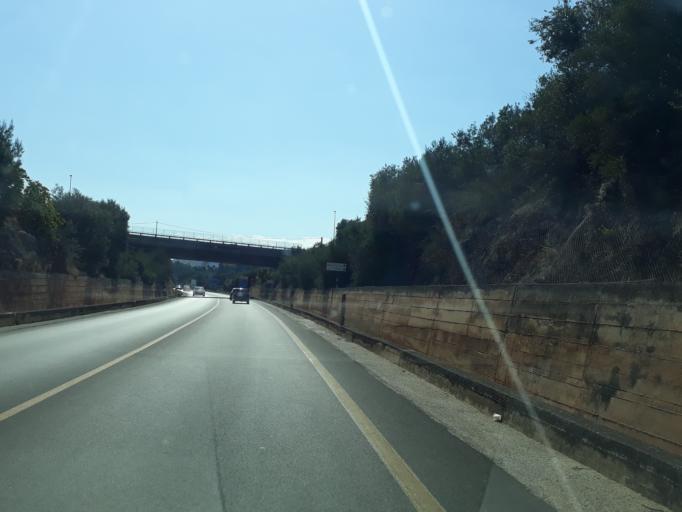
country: IT
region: Apulia
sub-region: Provincia di Brindisi
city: Fasano
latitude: 40.8354
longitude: 17.3501
